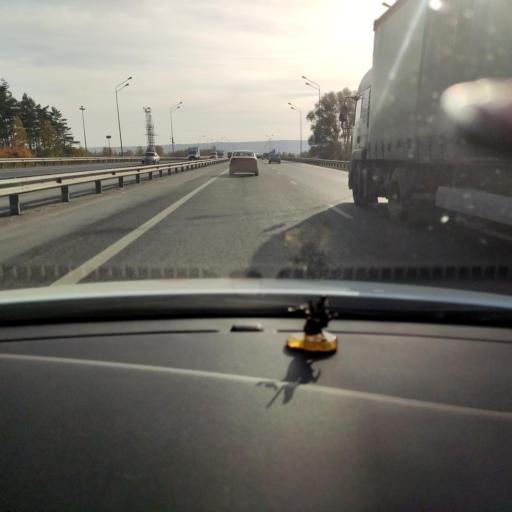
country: RU
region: Tatarstan
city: Osinovo
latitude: 55.8266
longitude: 48.8477
